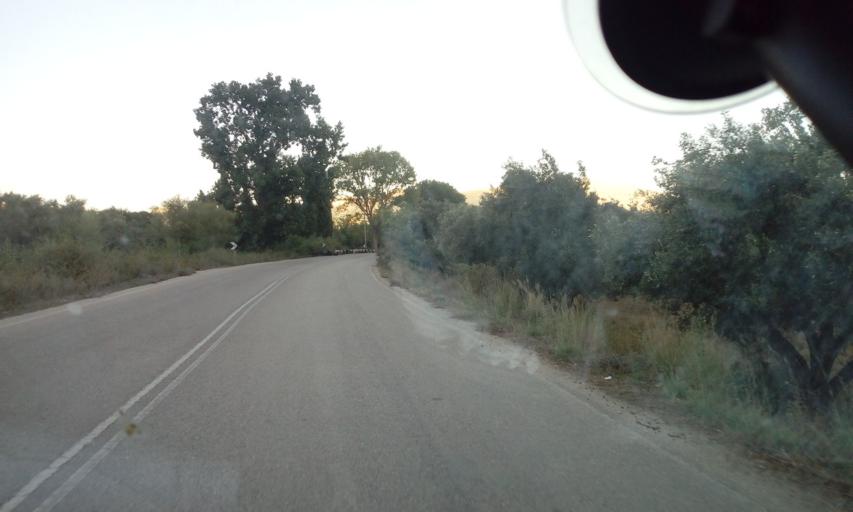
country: GR
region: West Greece
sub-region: Nomos Aitolias kai Akarnanias
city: Kandila
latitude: 38.6782
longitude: 20.9339
